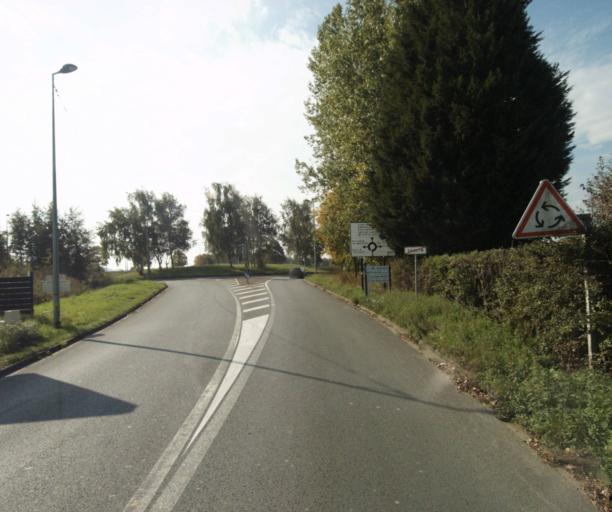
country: FR
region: Nord-Pas-de-Calais
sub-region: Departement du Nord
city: Seclin
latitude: 50.5434
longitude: 3.0434
